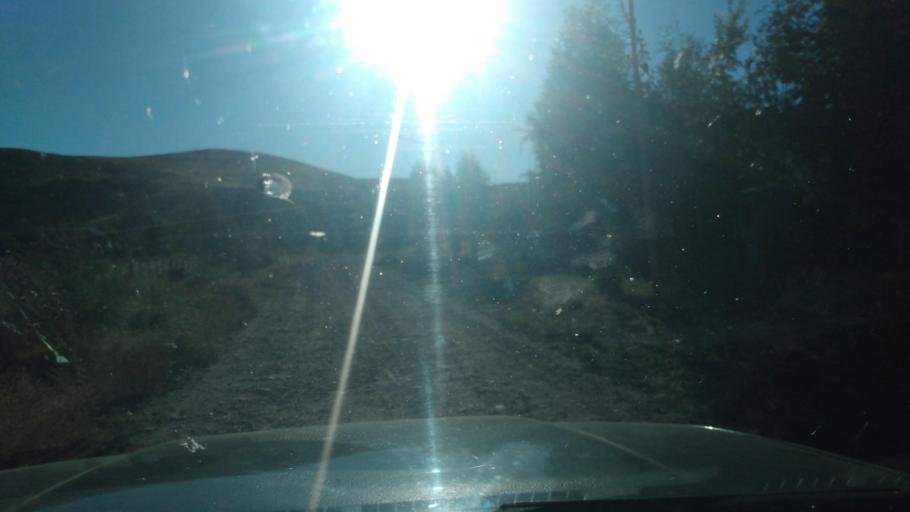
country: AR
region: Neuquen
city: Junin de los Andes
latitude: -39.9642
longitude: -71.0821
